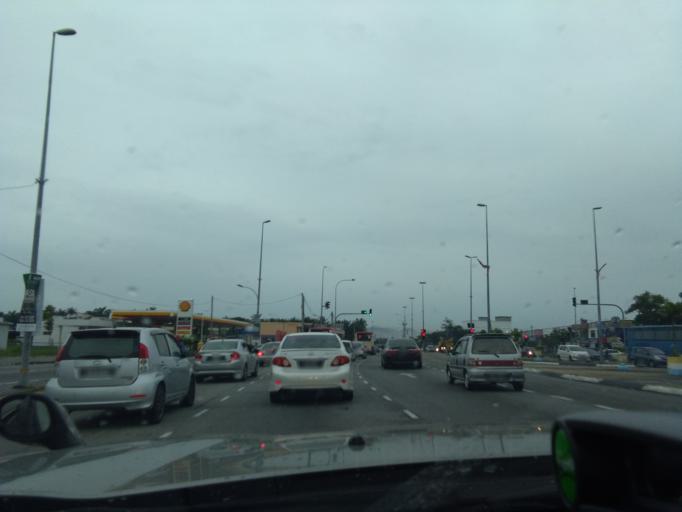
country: MY
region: Penang
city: Nibong Tebal
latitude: 5.1785
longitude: 100.4825
